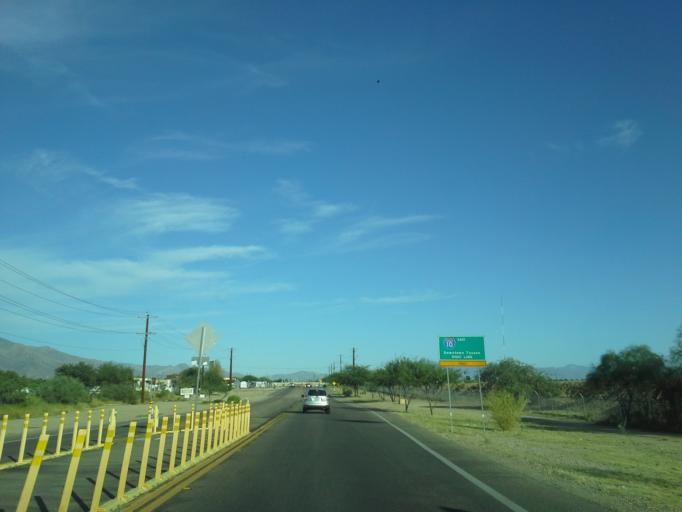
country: US
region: Arizona
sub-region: Pima County
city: Flowing Wells
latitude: 32.2942
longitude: -111.0364
